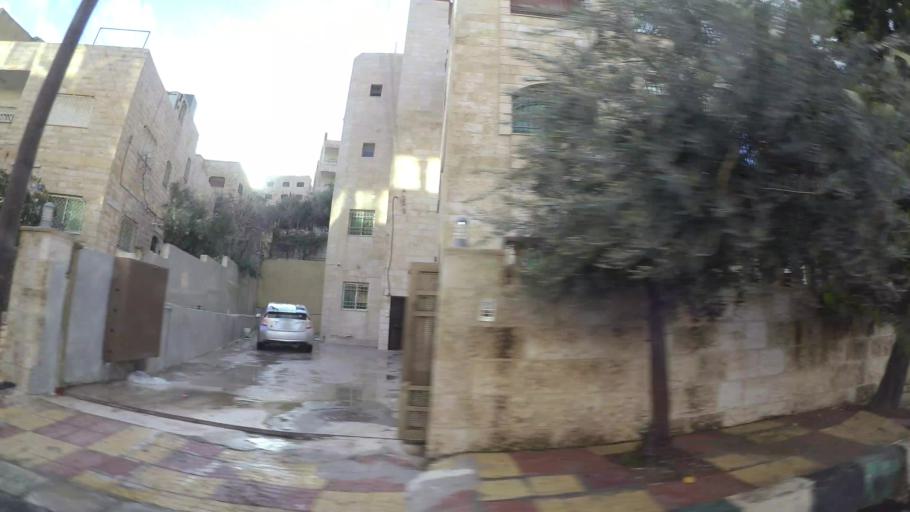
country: JO
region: Amman
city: Amman
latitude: 32.0030
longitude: 35.9216
